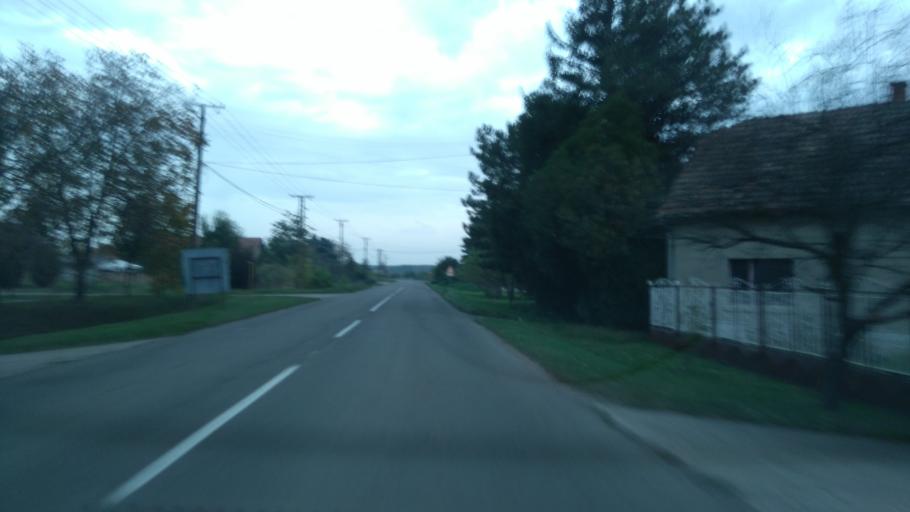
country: RS
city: Mol
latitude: 45.7741
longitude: 20.1319
